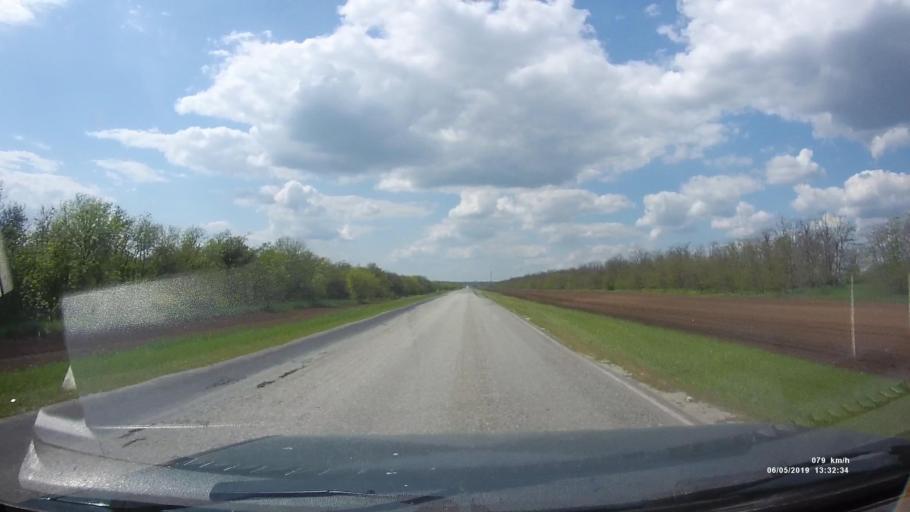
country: RU
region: Rostov
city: Ust'-Donetskiy
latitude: 47.6846
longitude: 40.7935
